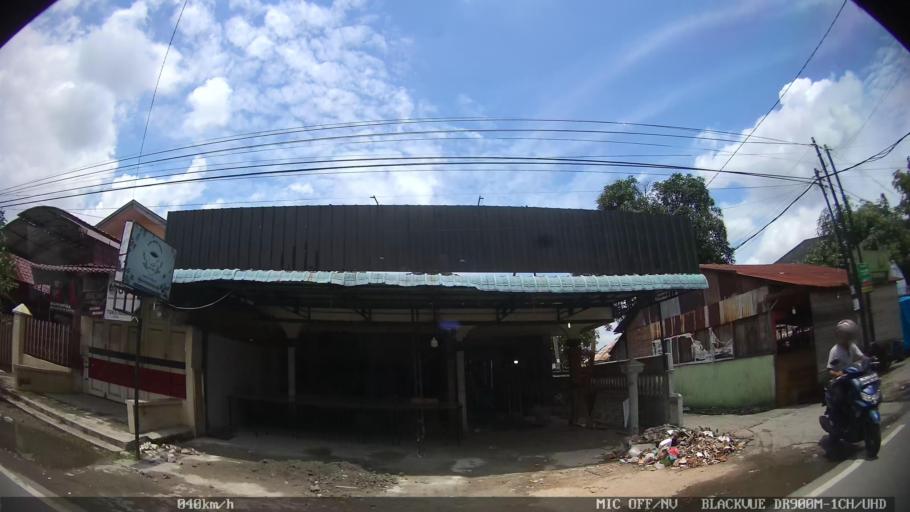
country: ID
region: North Sumatra
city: Medan
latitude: 3.6156
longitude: 98.7047
